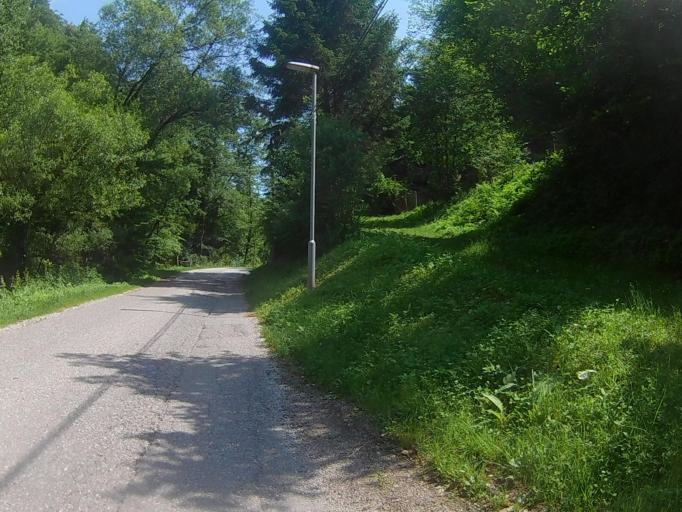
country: SI
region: Maribor
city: Bresternica
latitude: 46.5706
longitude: 15.5753
